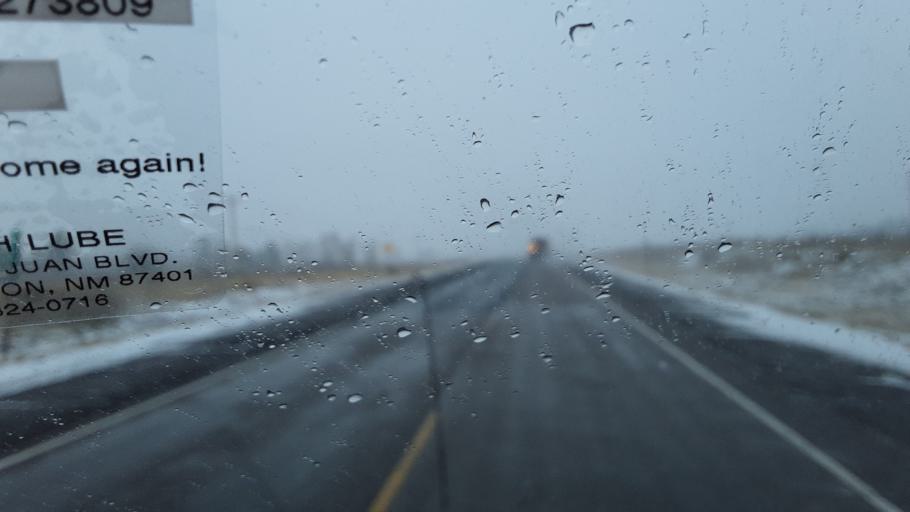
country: US
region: New Mexico
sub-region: Rio Arriba County
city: Chama
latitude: 36.8459
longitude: -106.5715
